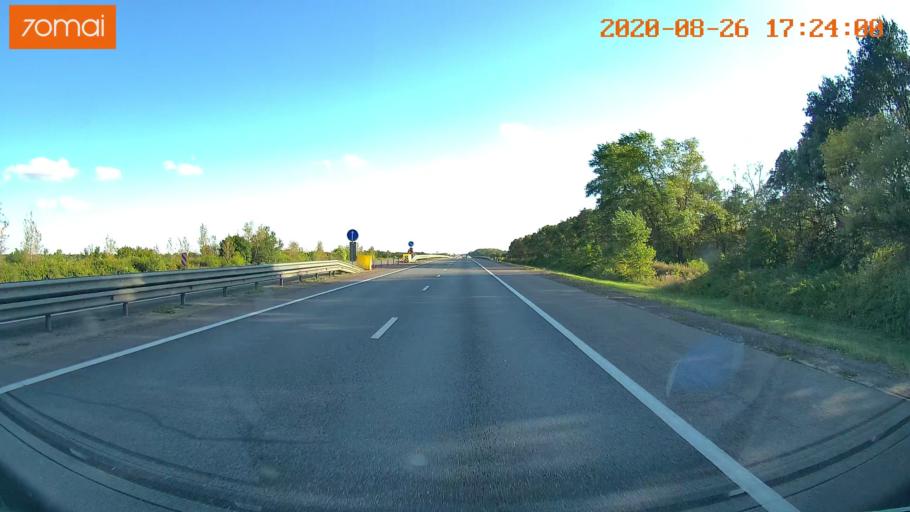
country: RU
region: Tula
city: Volovo
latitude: 53.5250
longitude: 38.1180
